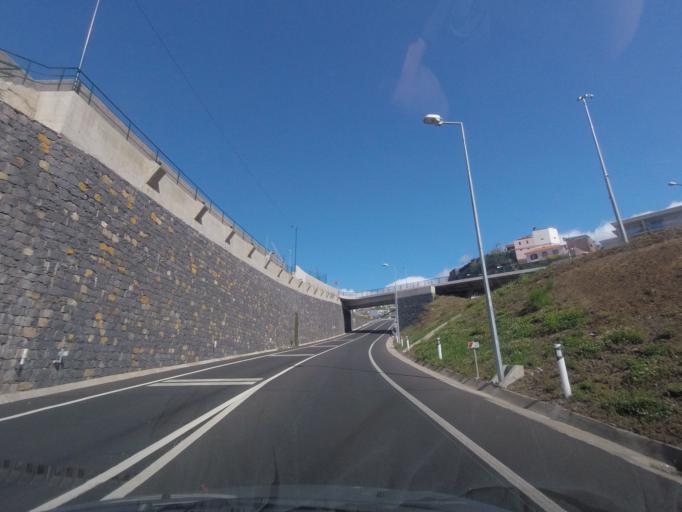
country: PT
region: Madeira
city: Camara de Lobos
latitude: 32.6555
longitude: -16.9682
